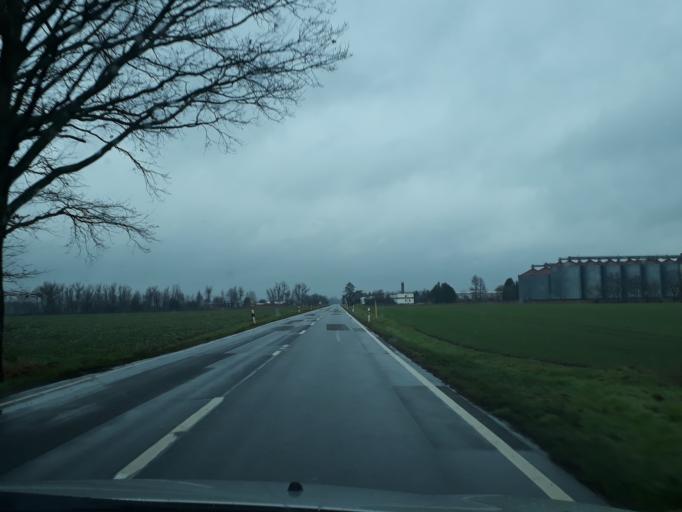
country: DE
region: Saxony
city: Malschwitz
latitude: 51.2454
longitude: 14.5368
